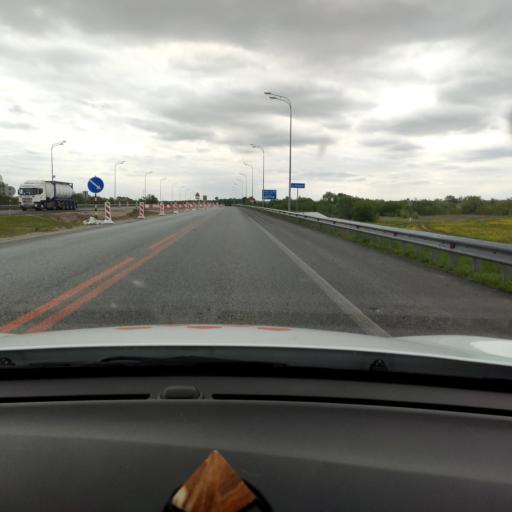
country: RU
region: Tatarstan
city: Pestretsy
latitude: 55.7020
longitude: 49.5740
